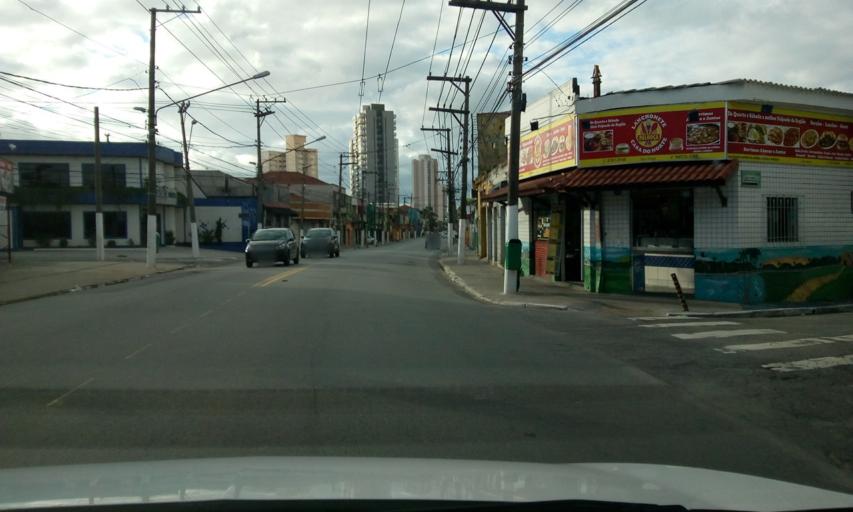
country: BR
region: Sao Paulo
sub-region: Sao Caetano Do Sul
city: Sao Caetano do Sul
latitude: -23.5571
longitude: -46.5247
